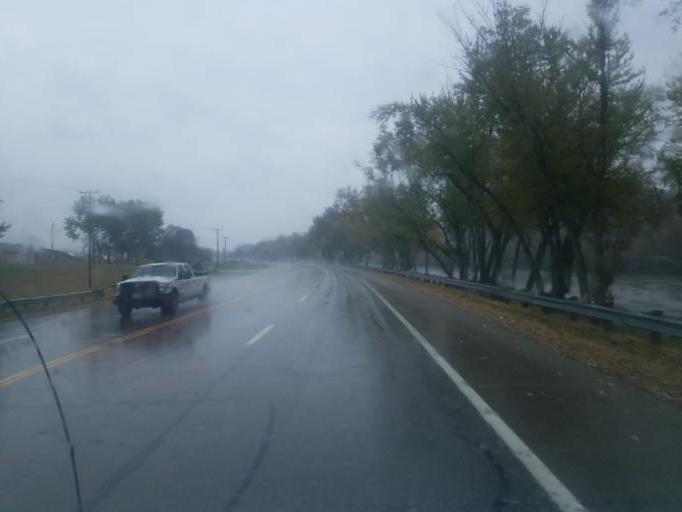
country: US
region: Ohio
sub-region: Muskingum County
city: South Zanesville
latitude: 39.8722
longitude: -81.9538
